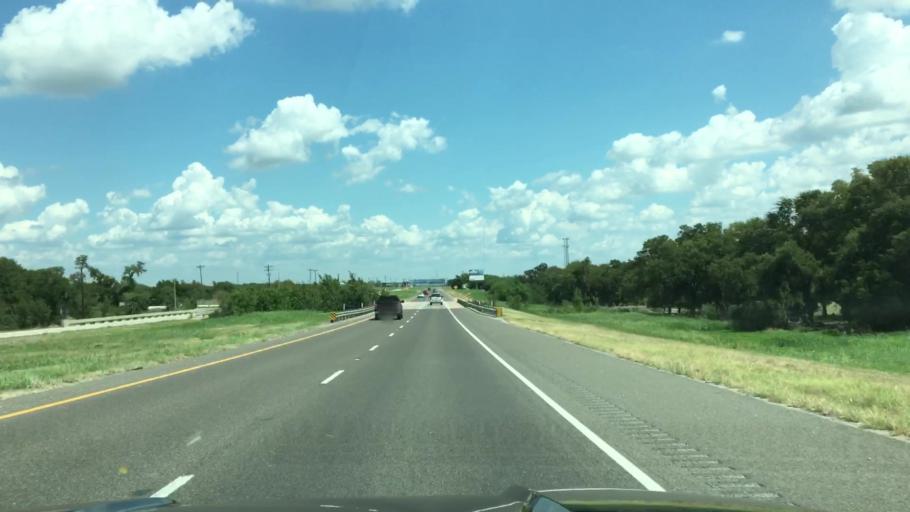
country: US
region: Texas
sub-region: Wise County
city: Rhome
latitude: 33.0366
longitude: -97.4065
